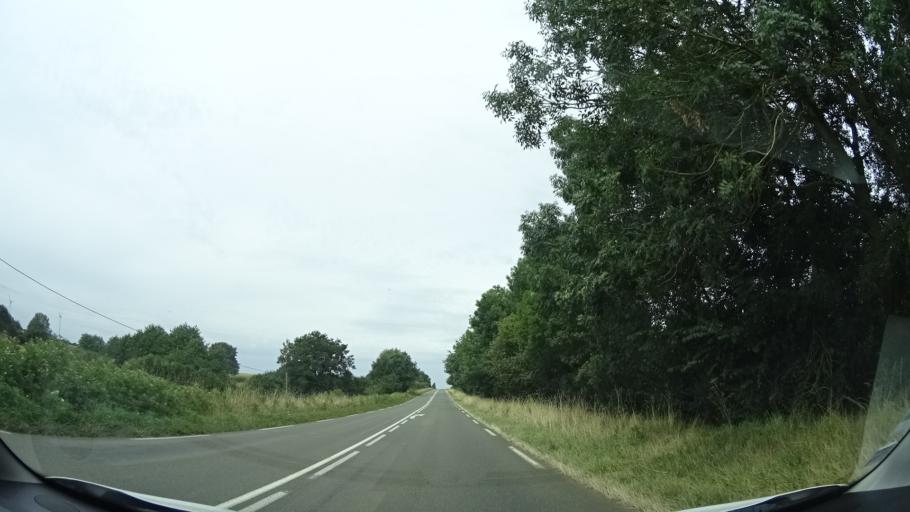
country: FR
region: Pays de la Loire
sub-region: Departement de la Mayenne
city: Meslay-du-Maine
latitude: 47.9168
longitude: -0.4696
